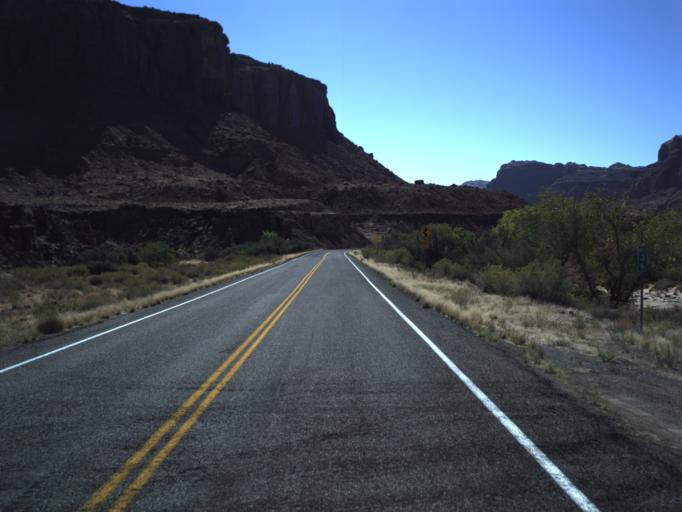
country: US
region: Utah
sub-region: San Juan County
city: Blanding
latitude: 37.9327
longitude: -110.4665
